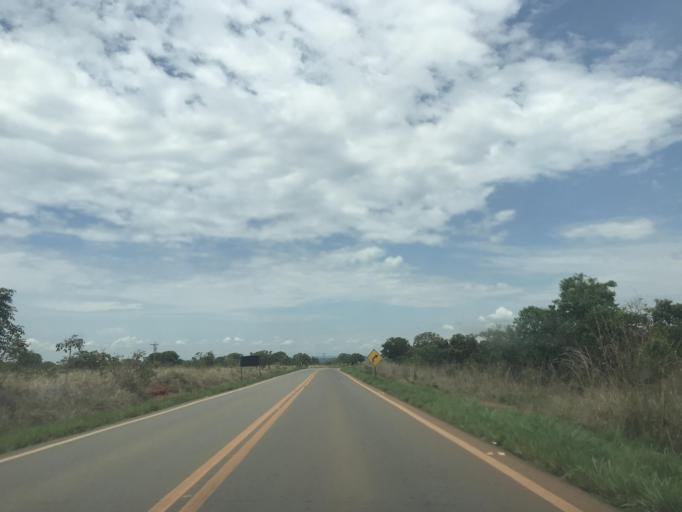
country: BR
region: Goias
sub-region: Luziania
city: Luziania
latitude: -16.3469
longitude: -48.0231
